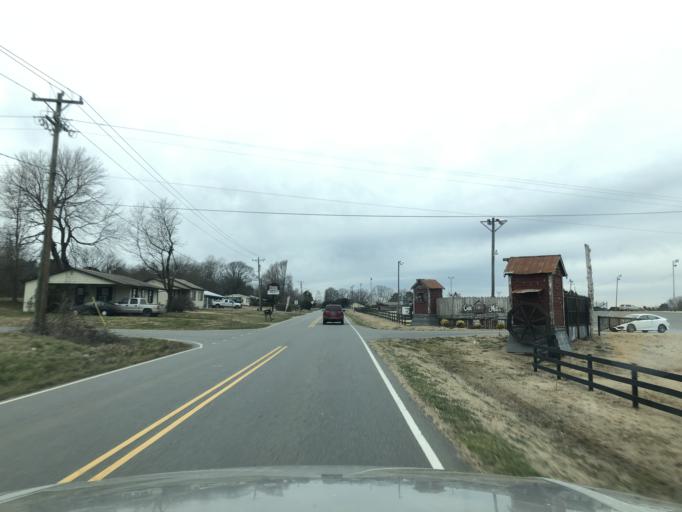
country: US
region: North Carolina
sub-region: Cleveland County
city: Shelby
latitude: 35.3363
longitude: -81.5022
